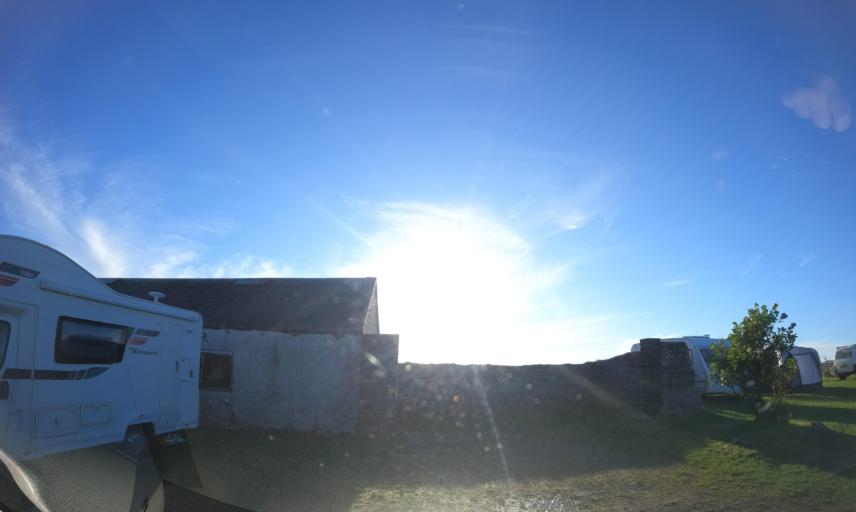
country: GB
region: Scotland
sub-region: Eilean Siar
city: Barra
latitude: 56.4780
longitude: -6.9219
